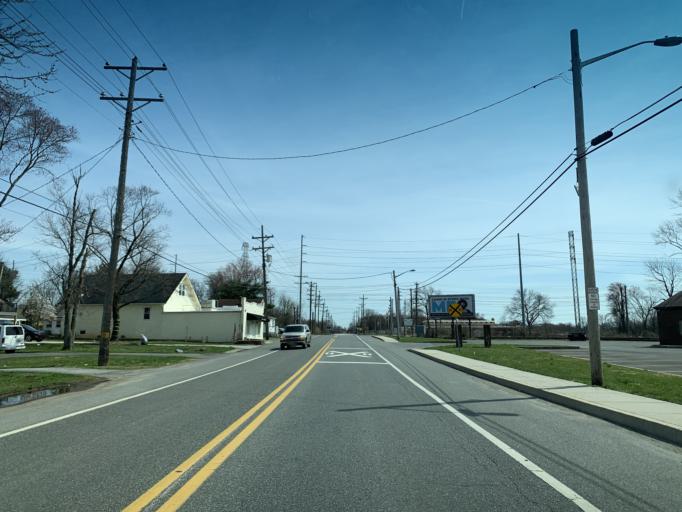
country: US
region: Delaware
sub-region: New Castle County
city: Newport
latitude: 39.7308
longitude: -75.6248
